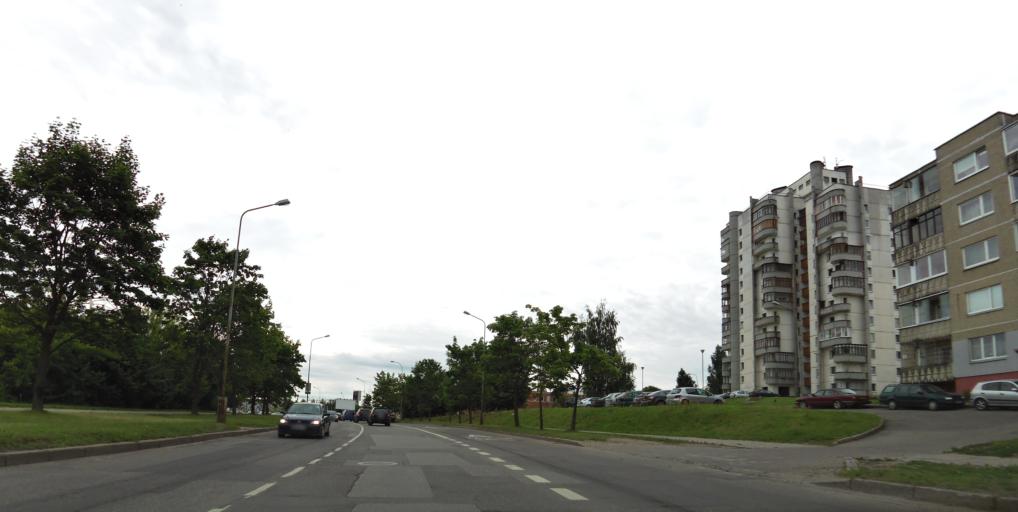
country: LT
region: Vilnius County
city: Seskine
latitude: 54.7127
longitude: 25.2562
